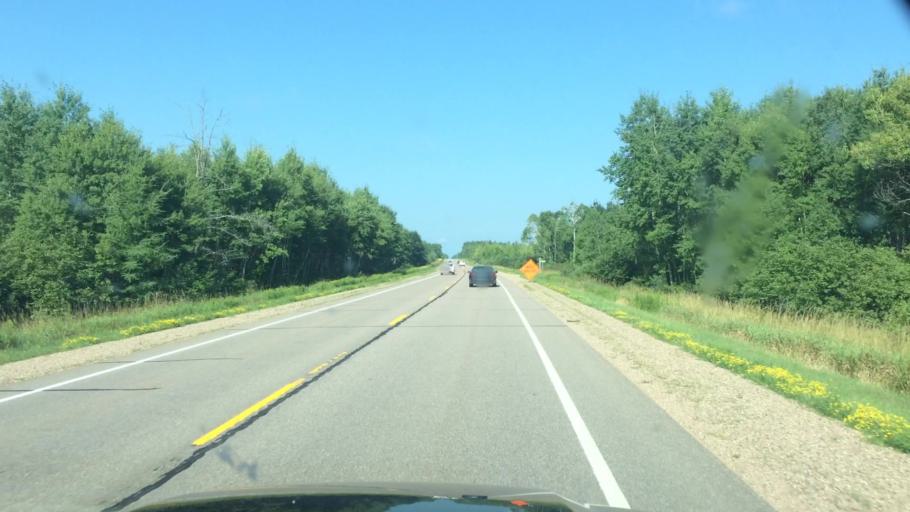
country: US
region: Wisconsin
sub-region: Langlade County
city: Antigo
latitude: 45.1467
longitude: -89.3425
